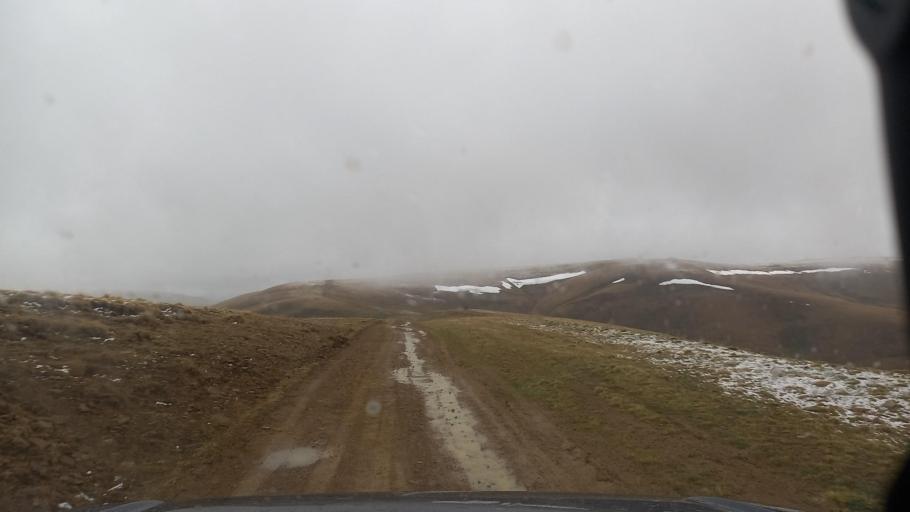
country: RU
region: Kabardino-Balkariya
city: Terskol
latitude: 43.5913
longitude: 42.4822
